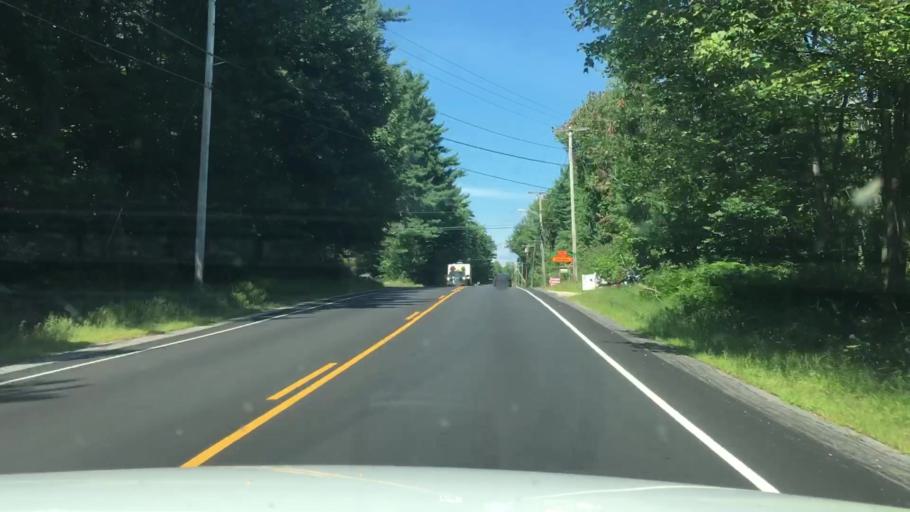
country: US
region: Maine
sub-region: Cumberland County
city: Cumberland Center
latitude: 43.8369
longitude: -70.3210
